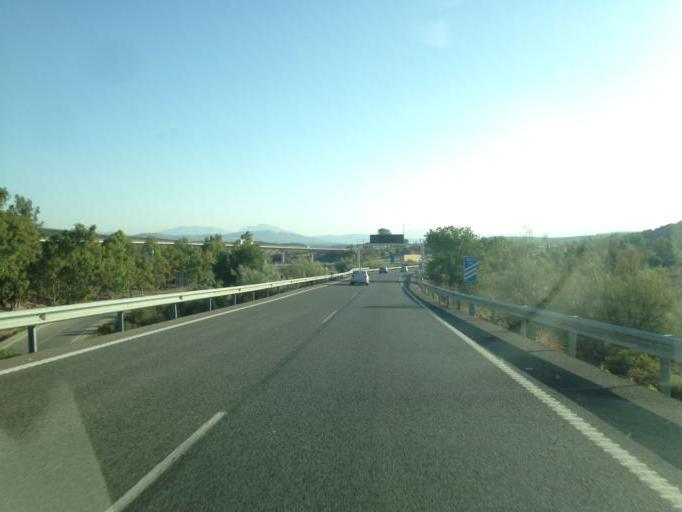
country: ES
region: Andalusia
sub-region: Provincia de Malaga
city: Villanueva de Tapia
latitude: 37.1256
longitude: -4.2914
